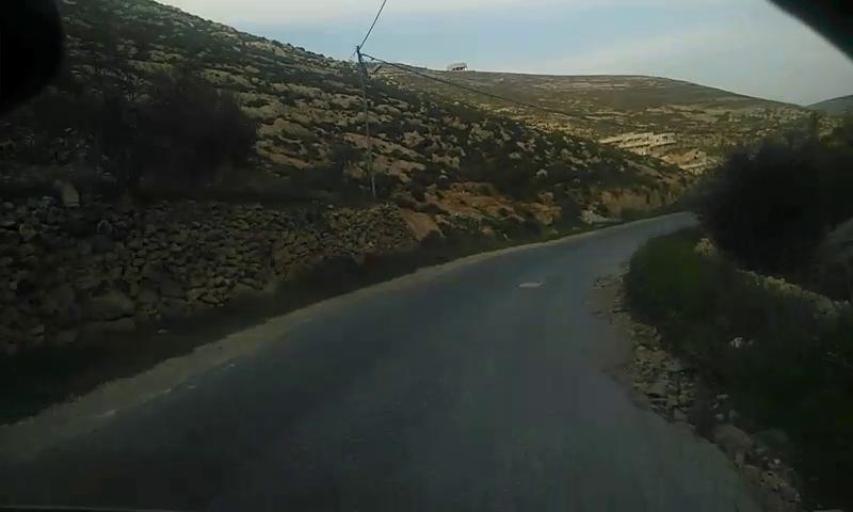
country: PS
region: West Bank
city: Ash Shuyukh
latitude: 31.5927
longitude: 35.1619
